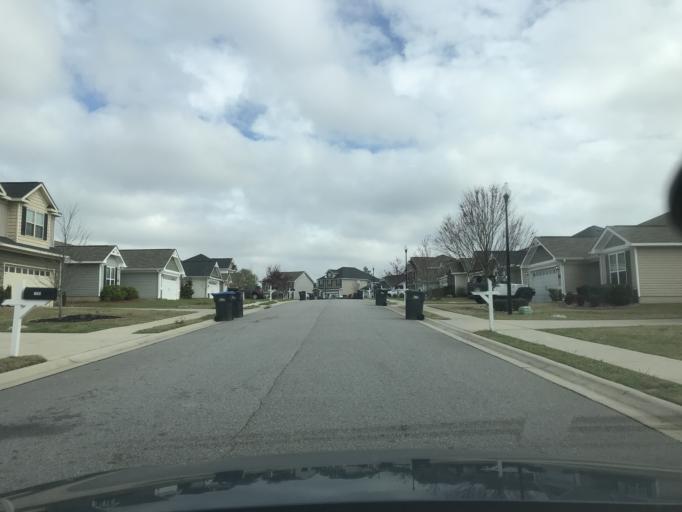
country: US
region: Georgia
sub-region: Columbia County
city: Grovetown
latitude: 33.4387
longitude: -82.1481
